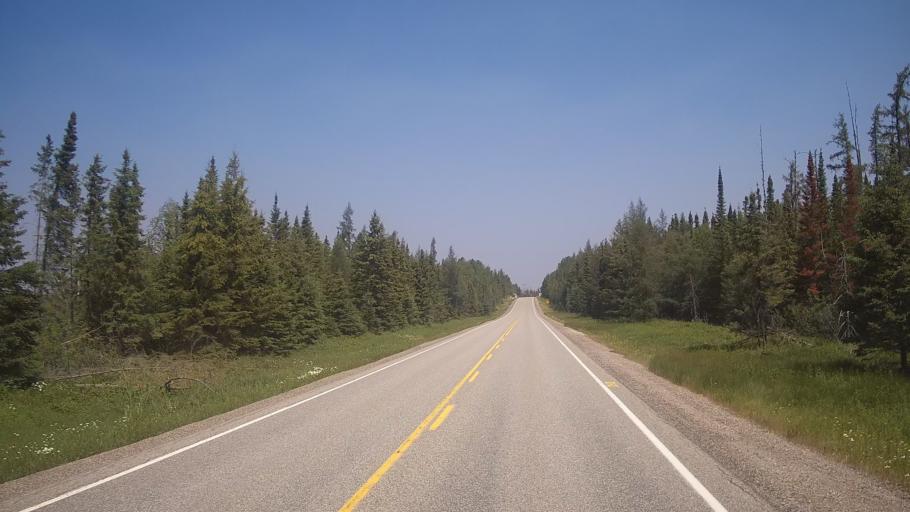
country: CA
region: Ontario
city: Timmins
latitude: 48.0397
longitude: -81.5831
